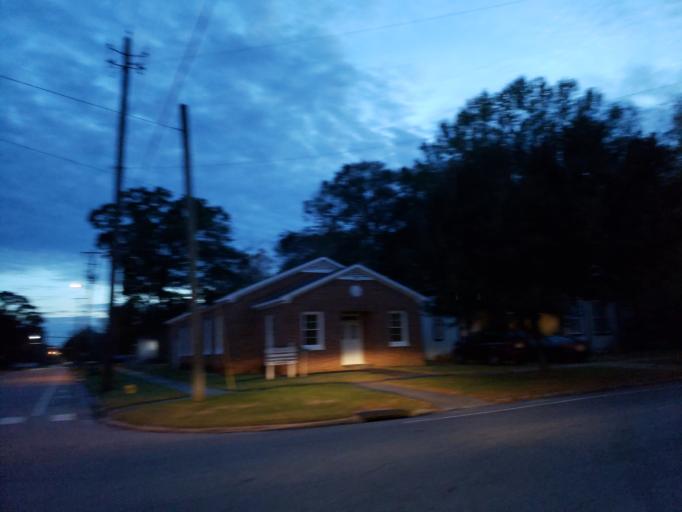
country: US
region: Mississippi
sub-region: Forrest County
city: Hattiesburg
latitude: 31.3229
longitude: -89.2916
